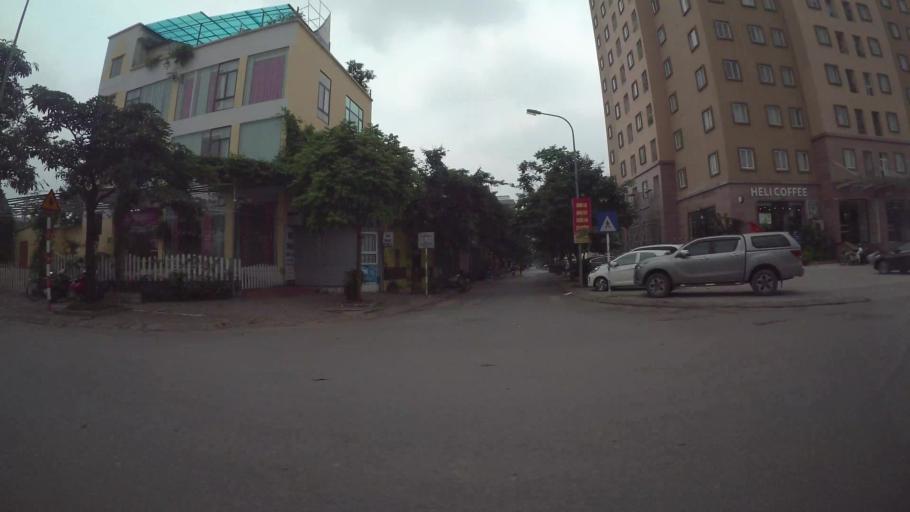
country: VN
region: Ha Noi
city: Trau Quy
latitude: 21.0594
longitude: 105.9145
